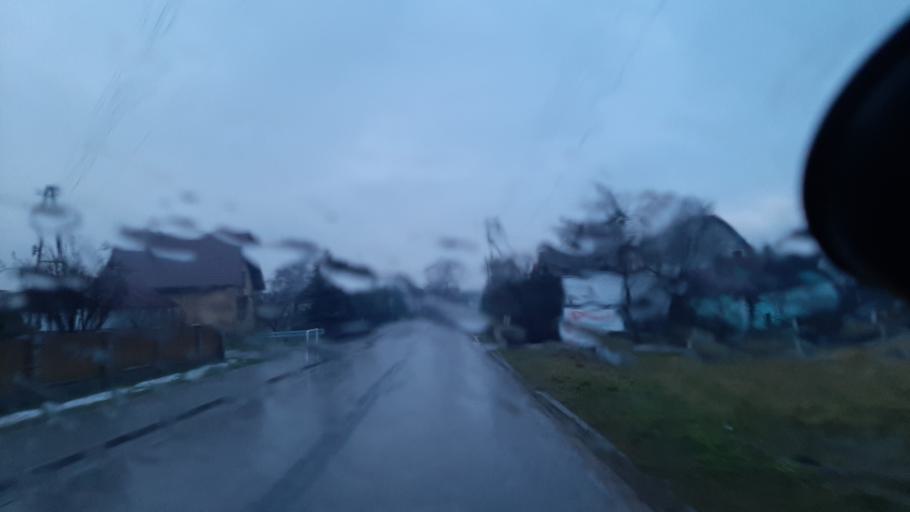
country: PL
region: Lublin Voivodeship
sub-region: Powiat lubartowski
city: Firlej
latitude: 51.5448
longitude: 22.5640
